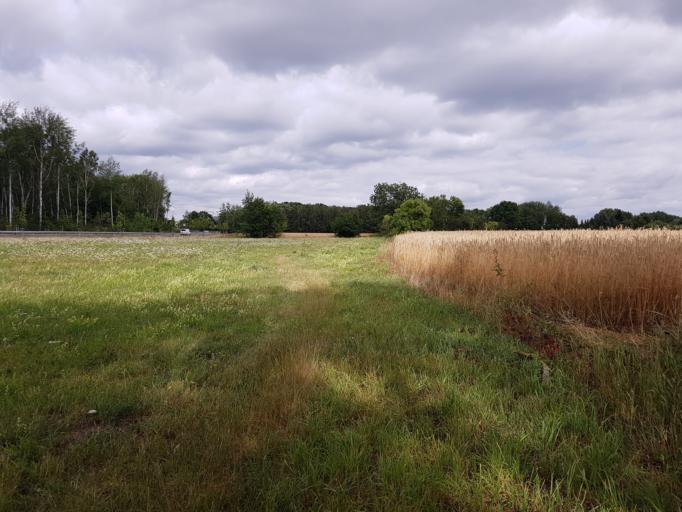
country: DE
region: Brandenburg
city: Finsterwalde
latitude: 51.6267
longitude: 13.7238
